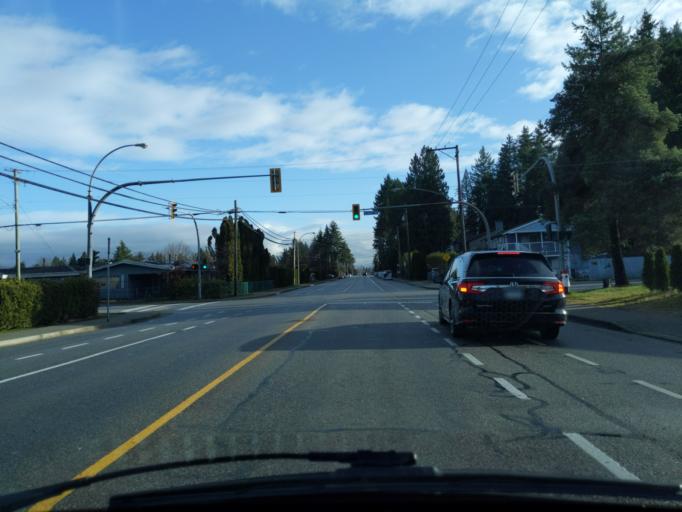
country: CA
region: British Columbia
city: Pitt Meadows
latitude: 49.2172
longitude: -122.6843
